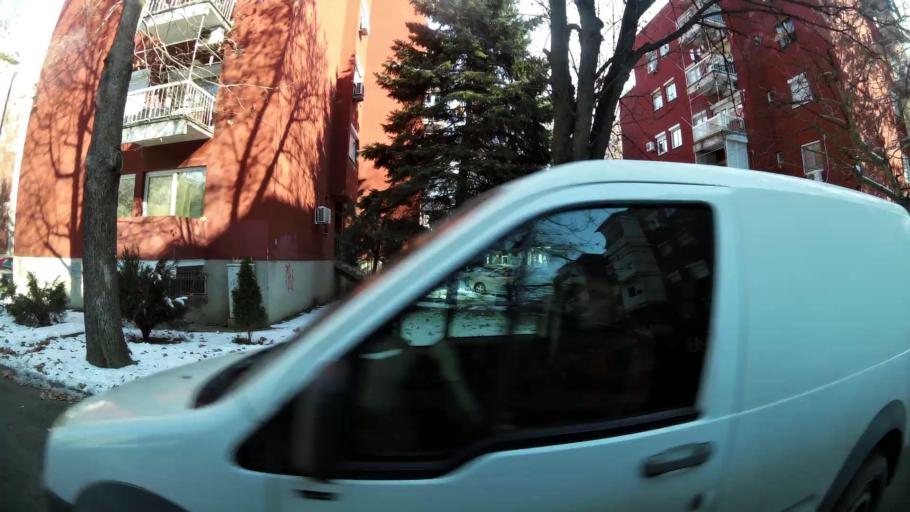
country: MK
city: Krushopek
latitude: 42.0038
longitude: 21.3722
